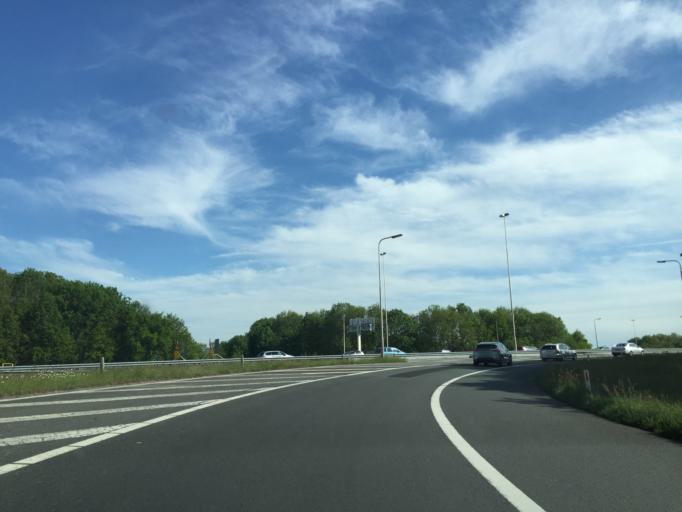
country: NL
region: Utrecht
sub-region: Gemeente Amersfoort
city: Randenbroek
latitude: 52.1774
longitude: 5.4291
